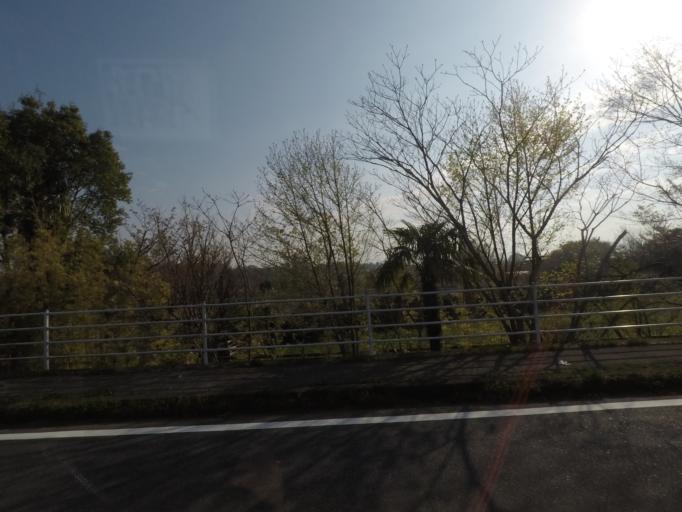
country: JP
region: Chiba
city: Shisui
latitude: 35.7196
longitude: 140.3142
